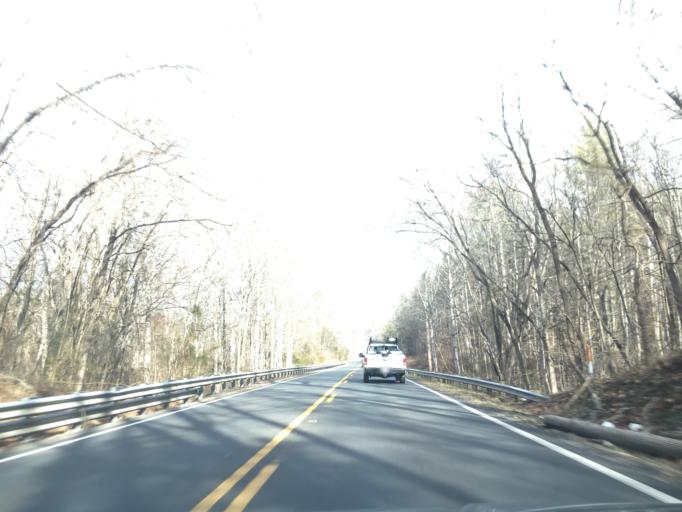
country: US
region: Virginia
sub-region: Culpeper County
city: Culpeper
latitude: 38.6117
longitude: -77.9507
